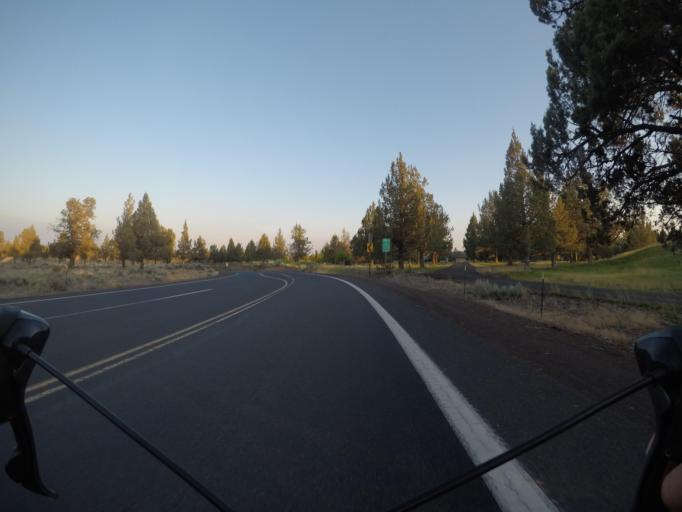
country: US
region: Oregon
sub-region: Deschutes County
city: Redmond
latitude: 44.2745
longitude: -121.2627
